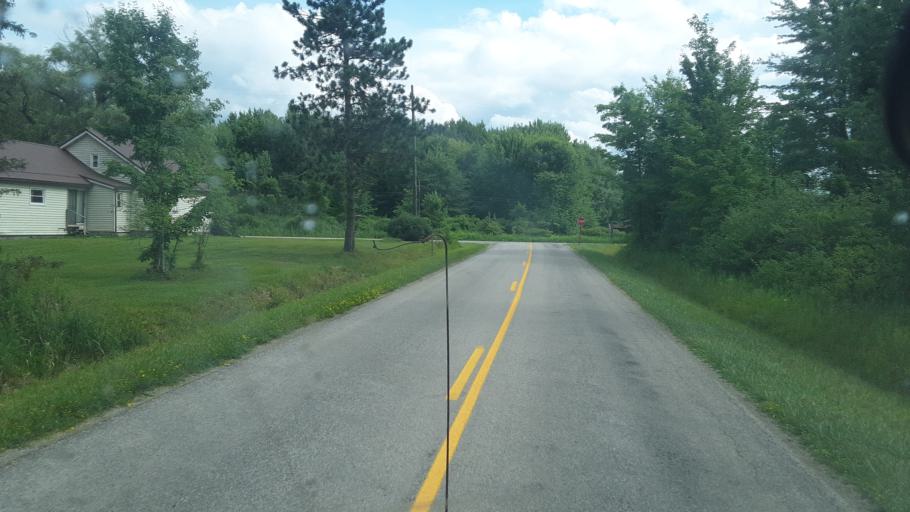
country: US
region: Ohio
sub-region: Ashtabula County
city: Roaming Shores
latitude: 41.6067
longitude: -80.7219
